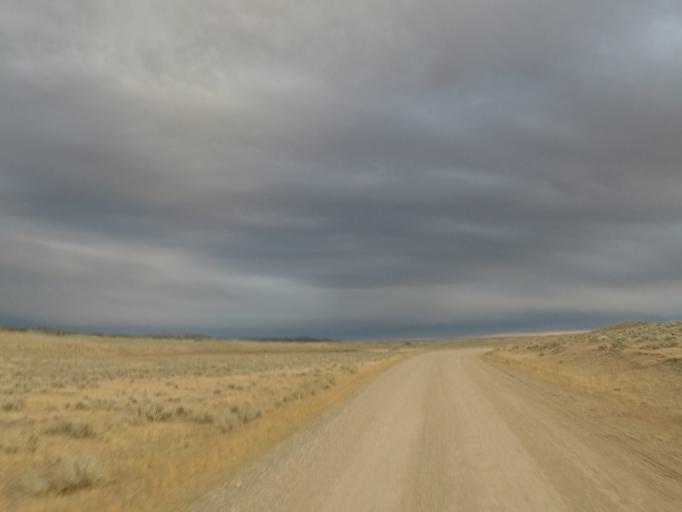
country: US
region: Montana
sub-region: Golden Valley County
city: Ryegate
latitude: 46.4295
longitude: -109.2513
